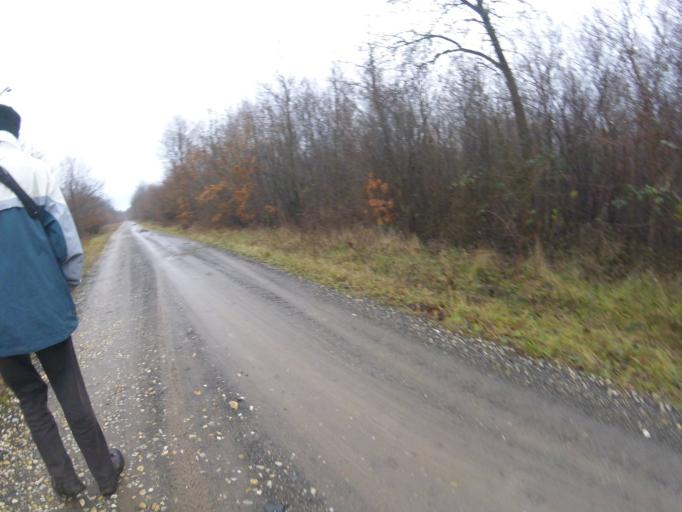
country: HU
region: Vas
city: Sarvar
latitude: 47.2358
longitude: 17.0021
